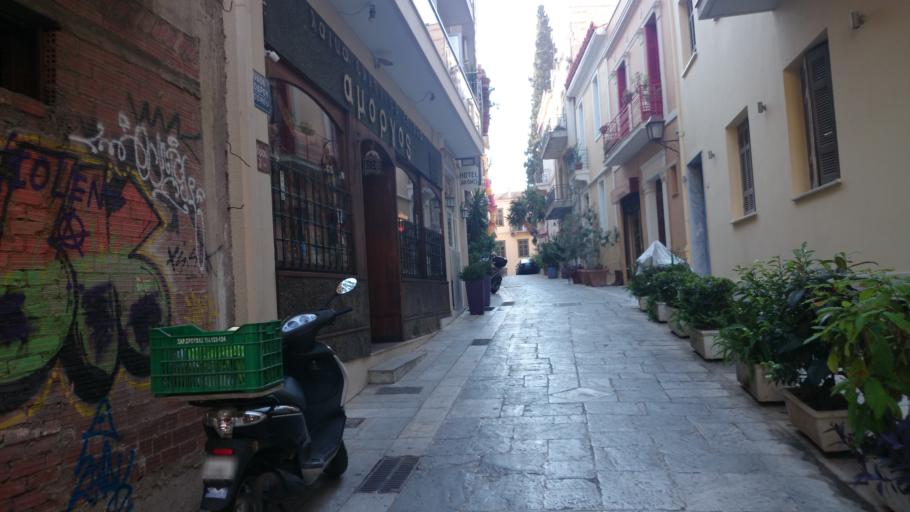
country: GR
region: Attica
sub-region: Nomarchia Athinas
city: Athens
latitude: 37.9734
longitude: 23.7322
